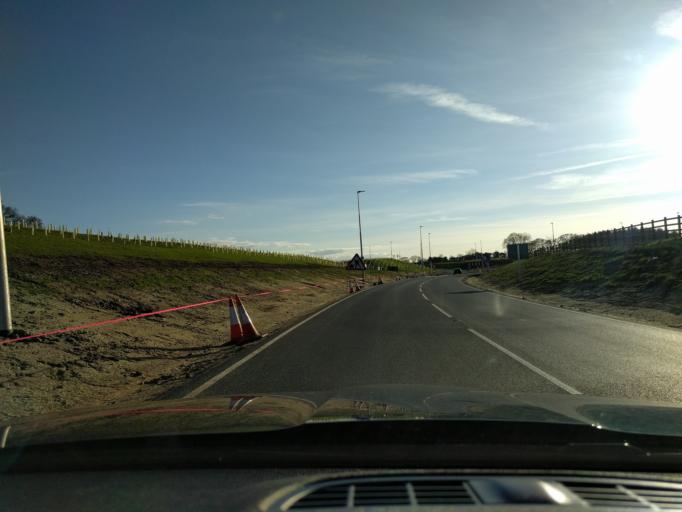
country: GB
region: England
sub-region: Northumberland
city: Morpeth
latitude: 55.1764
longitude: -1.7158
